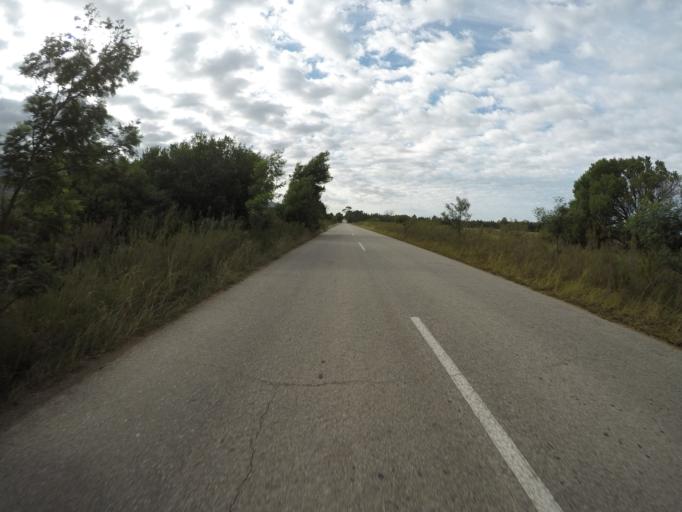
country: ZA
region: Eastern Cape
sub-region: Cacadu District Municipality
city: Kareedouw
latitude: -34.0436
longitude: 24.4273
